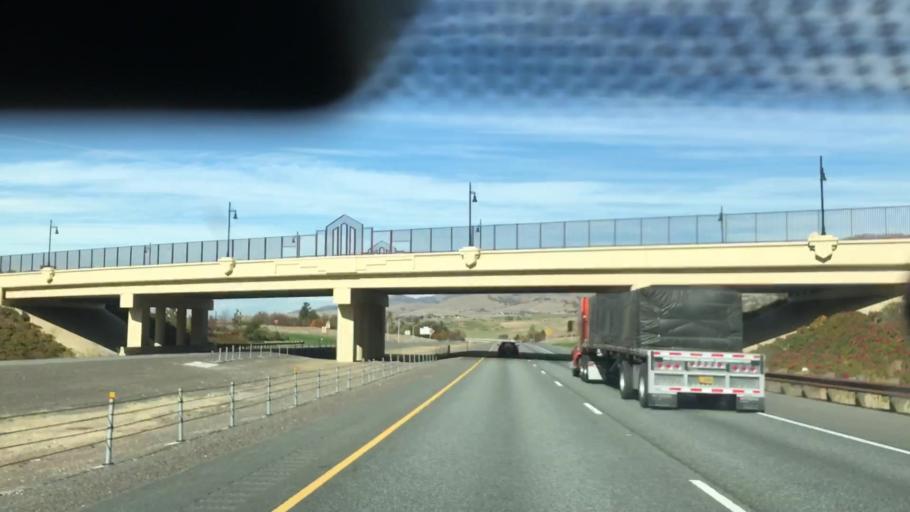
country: US
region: Oregon
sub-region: Jackson County
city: Ashland
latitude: 42.1867
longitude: -122.6664
